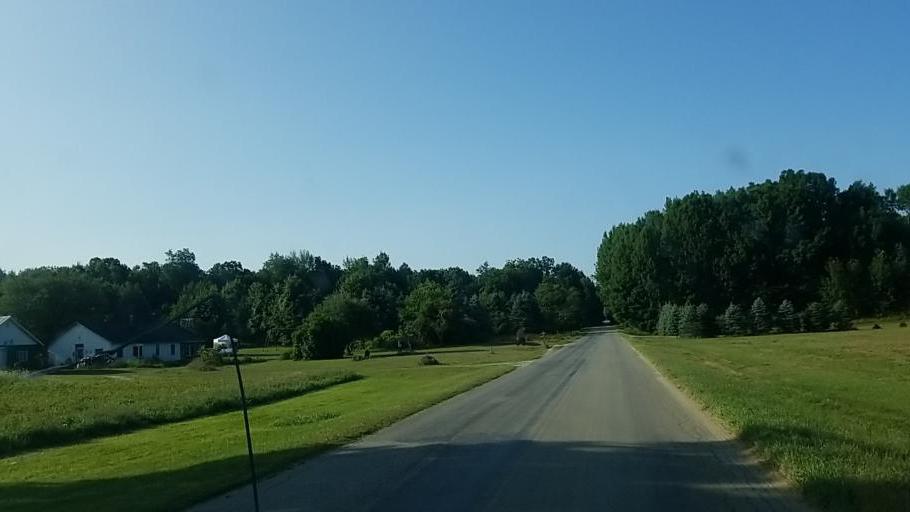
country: US
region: Michigan
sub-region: Newaygo County
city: Newaygo
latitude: 43.3780
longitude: -85.8307
